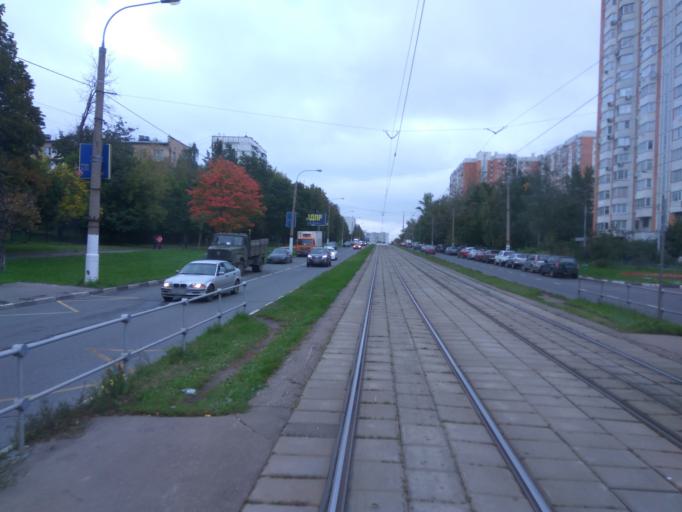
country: RU
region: Moscow
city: Kotlovka
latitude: 55.6494
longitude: 37.6055
